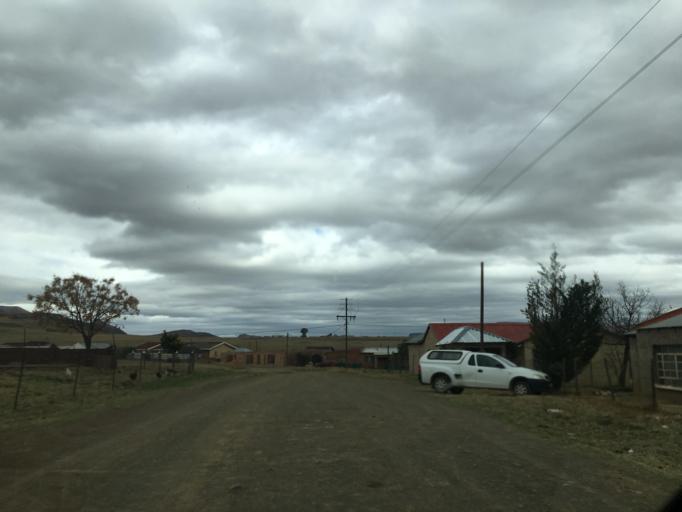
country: ZA
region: Eastern Cape
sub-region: Chris Hani District Municipality
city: Cala
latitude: -31.5372
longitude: 27.6908
